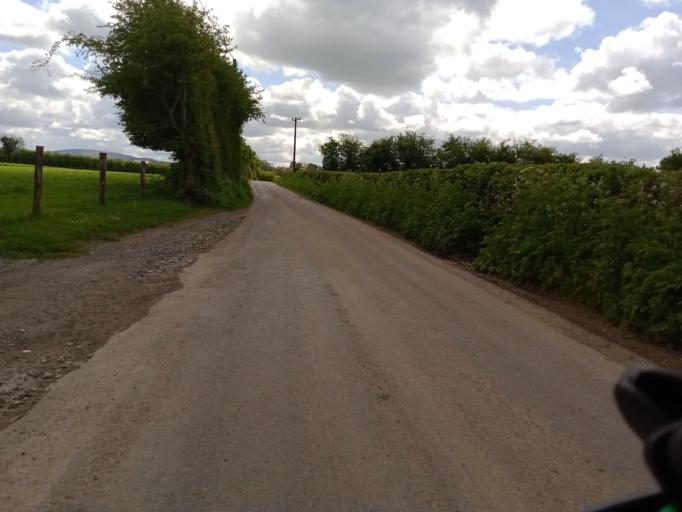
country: IE
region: Leinster
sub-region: Kilkenny
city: Thomastown
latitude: 52.5959
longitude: -7.1522
